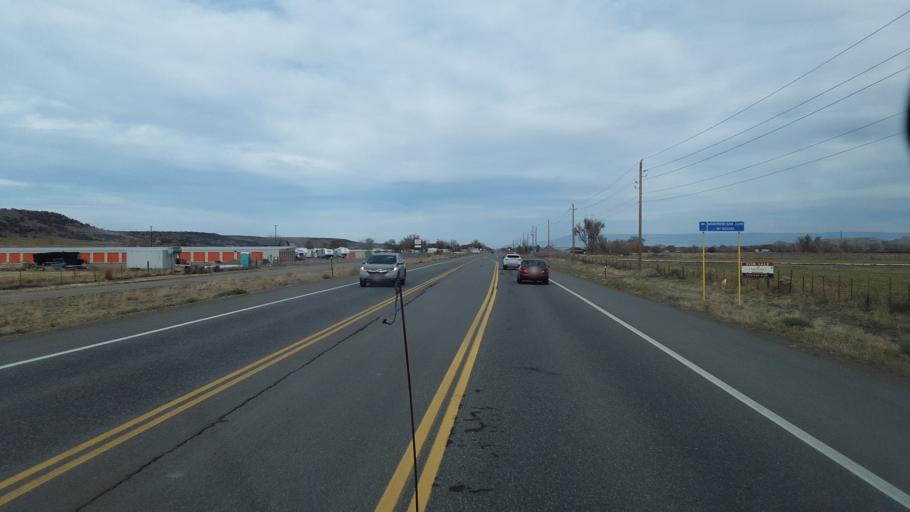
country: US
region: Colorado
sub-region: Montrose County
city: Montrose
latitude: 38.3573
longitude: -107.8008
